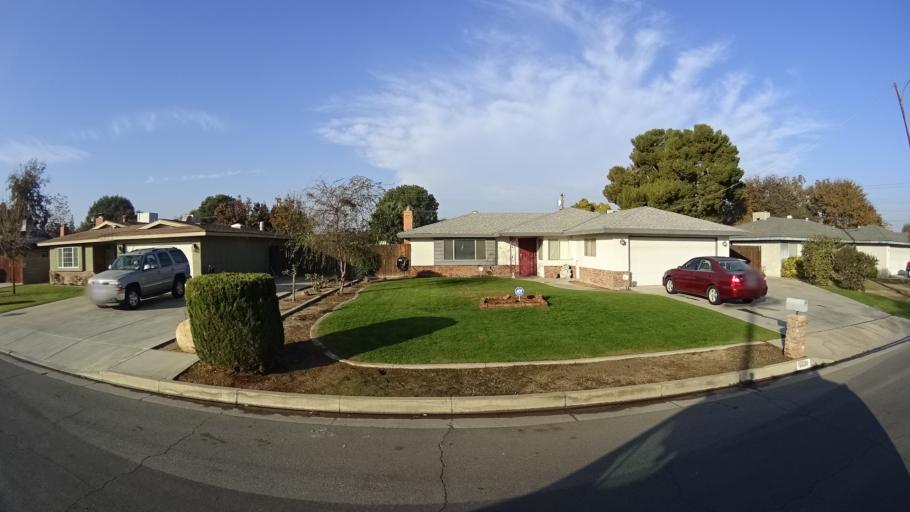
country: US
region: California
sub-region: Kern County
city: Greenacres
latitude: 35.3852
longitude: -119.1189
